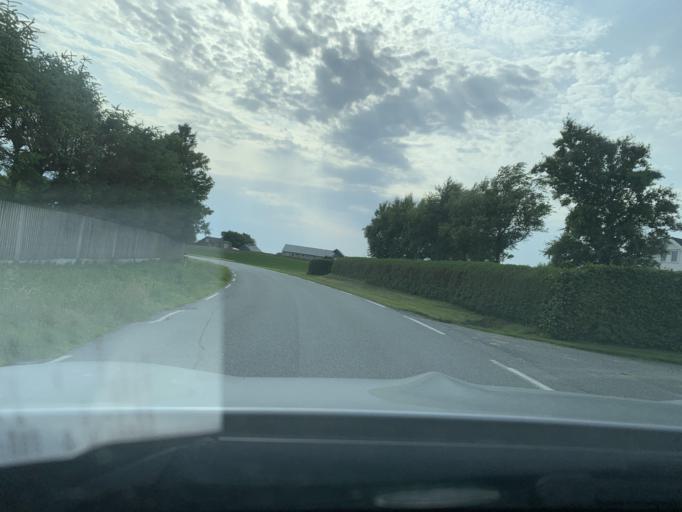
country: NO
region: Rogaland
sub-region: Time
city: Bryne
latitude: 58.7332
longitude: 5.5953
